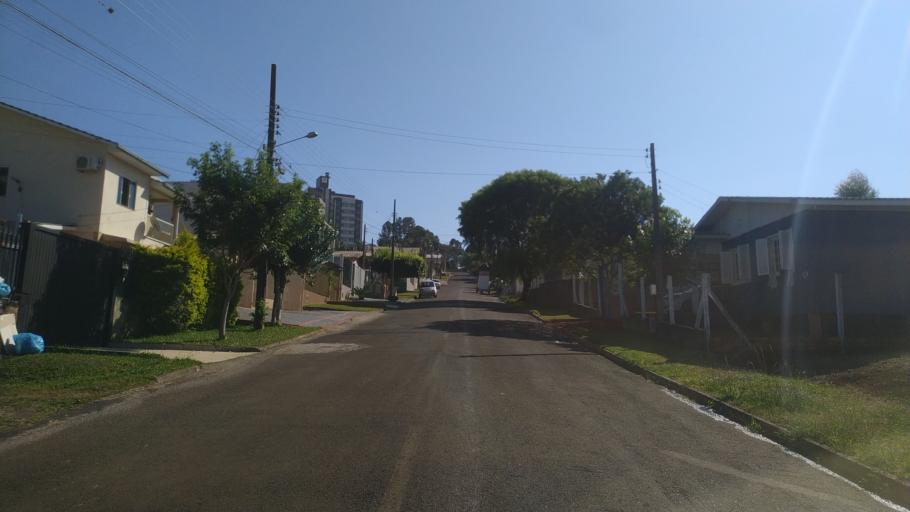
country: BR
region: Santa Catarina
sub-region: Chapeco
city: Chapeco
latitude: -27.0759
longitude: -52.6077
